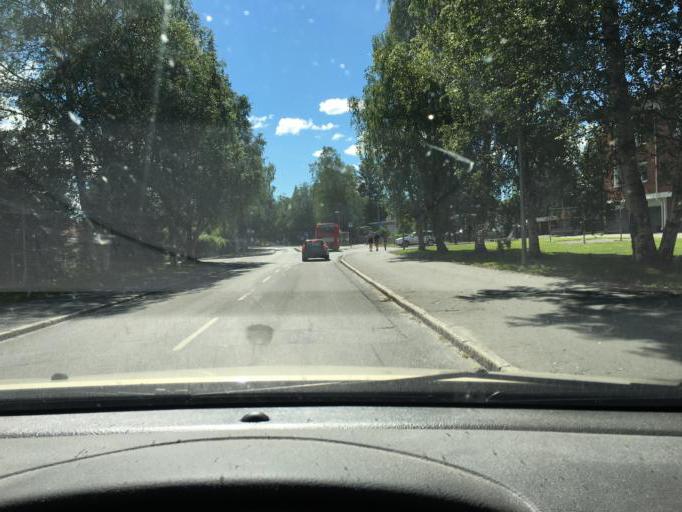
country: SE
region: Norrbotten
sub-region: Lulea Kommun
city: Lulea
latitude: 65.5981
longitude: 22.1345
